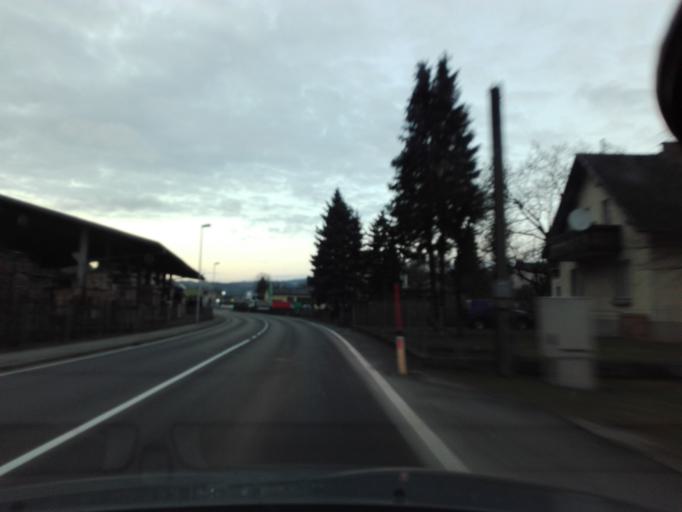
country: AT
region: Upper Austria
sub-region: Politischer Bezirk Perg
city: Bad Kreuzen
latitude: 48.2196
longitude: 14.8537
